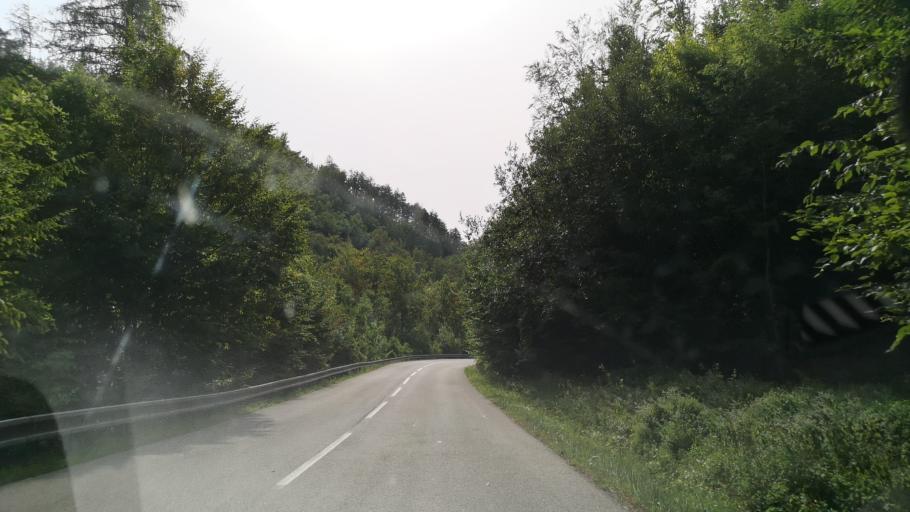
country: SK
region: Banskobystricky
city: Tisovec
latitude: 48.5824
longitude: 20.0123
